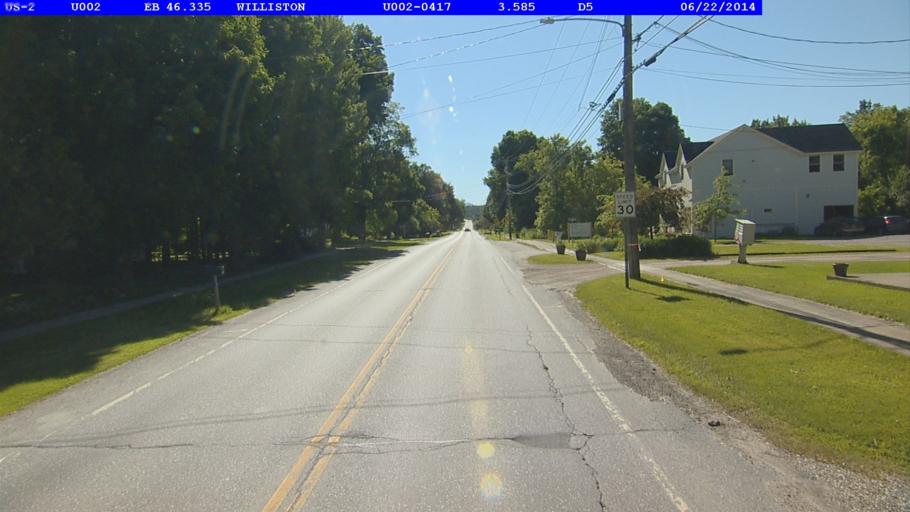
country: US
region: Vermont
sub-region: Chittenden County
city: Williston
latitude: 44.4381
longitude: -73.0713
